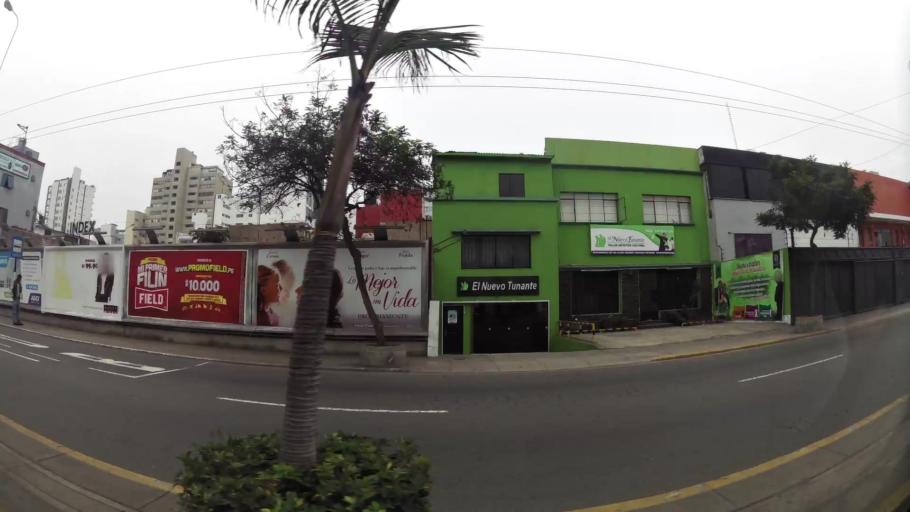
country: PE
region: Lima
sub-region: Lima
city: San Isidro
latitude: -12.1150
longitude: -77.0466
